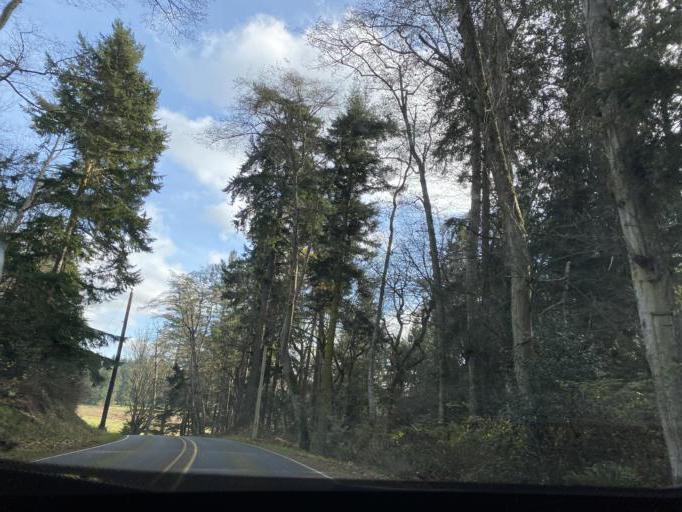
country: US
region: Washington
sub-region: Island County
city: Freeland
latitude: 47.9779
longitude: -122.4600
